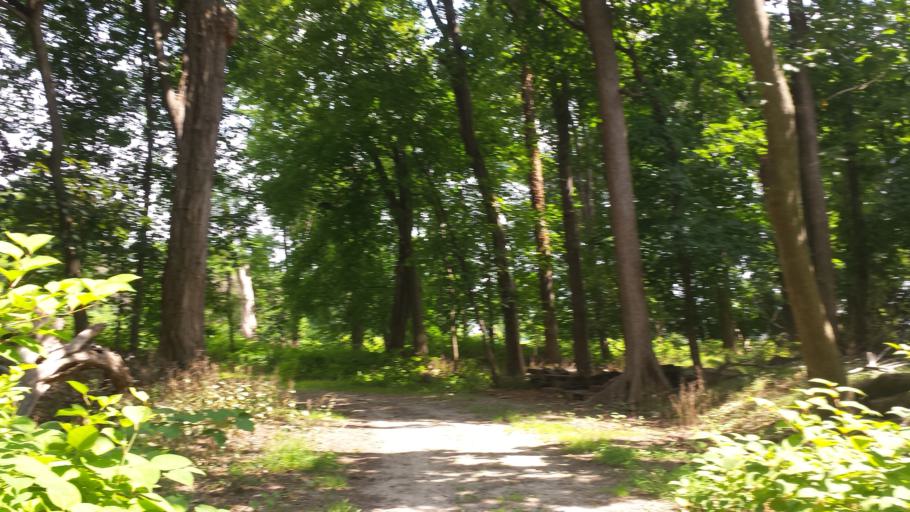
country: US
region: New York
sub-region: Westchester County
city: Rye
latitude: 40.9696
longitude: -73.6633
